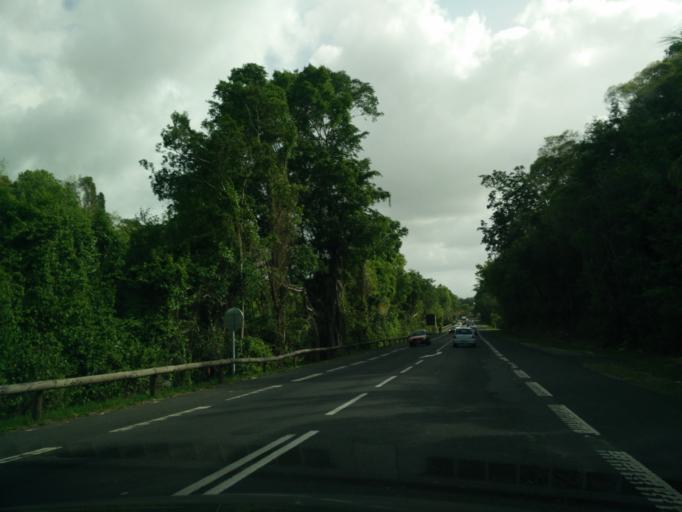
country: GP
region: Guadeloupe
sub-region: Guadeloupe
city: Les Abymes
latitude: 16.3196
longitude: -61.4772
